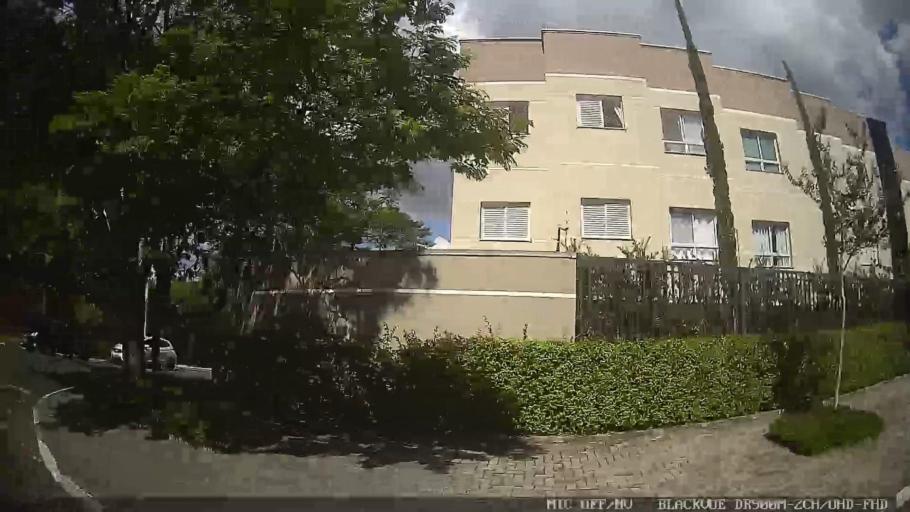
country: BR
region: Sao Paulo
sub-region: Atibaia
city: Atibaia
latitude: -23.1273
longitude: -46.5527
